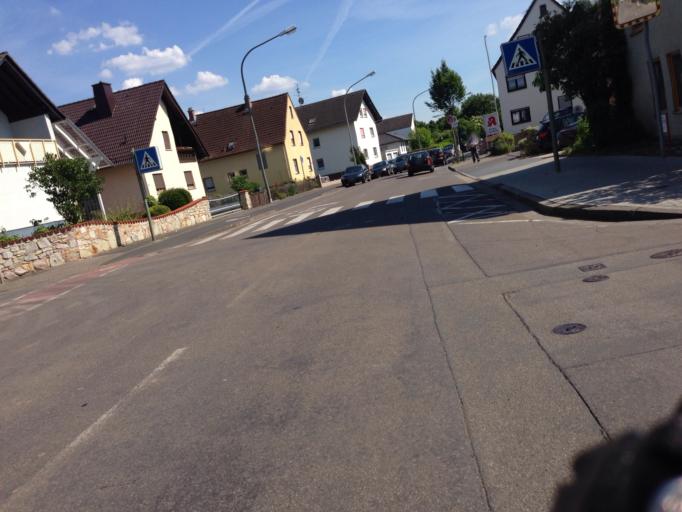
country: DE
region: Hesse
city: Bruchkobel
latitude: 50.1771
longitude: 8.8891
